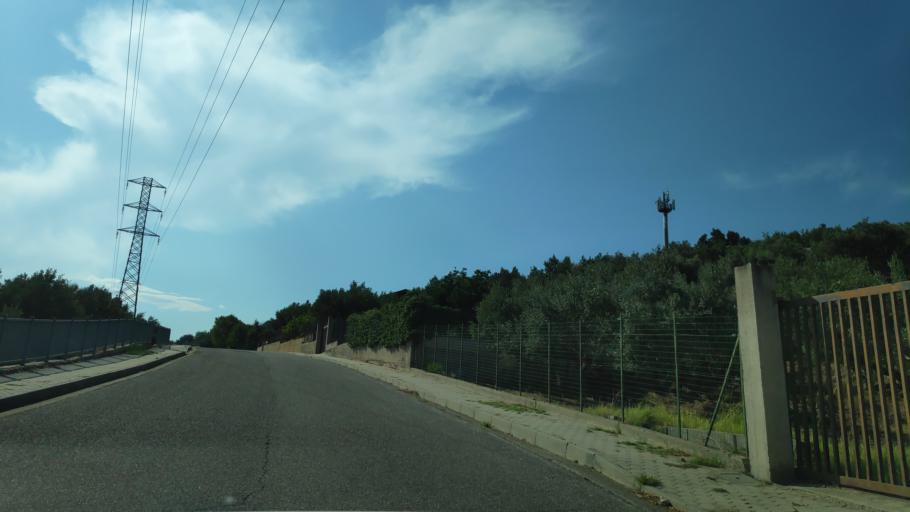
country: IT
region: Calabria
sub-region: Provincia di Catanzaro
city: Martelli-Laganosa
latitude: 38.6853
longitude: 16.5402
